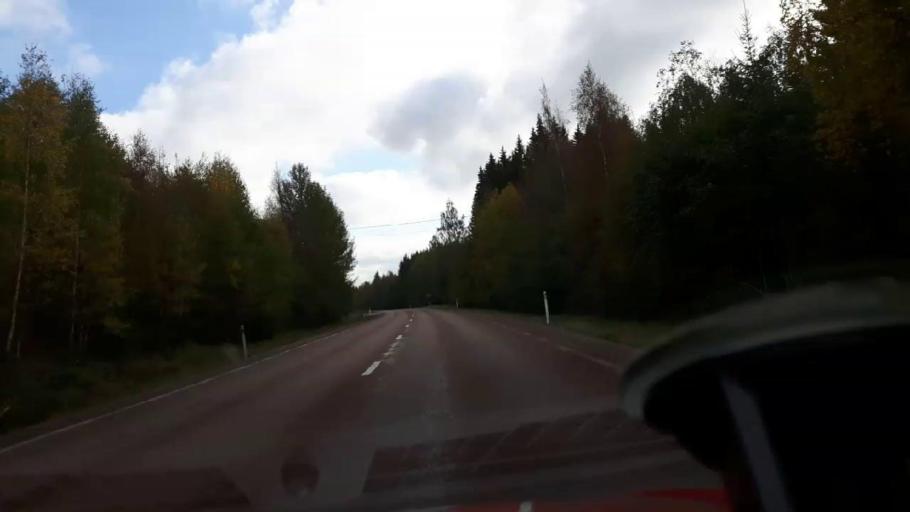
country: SE
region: Gaevleborg
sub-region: Ljusdals Kommun
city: Jaervsoe
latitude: 61.6390
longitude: 16.2387
